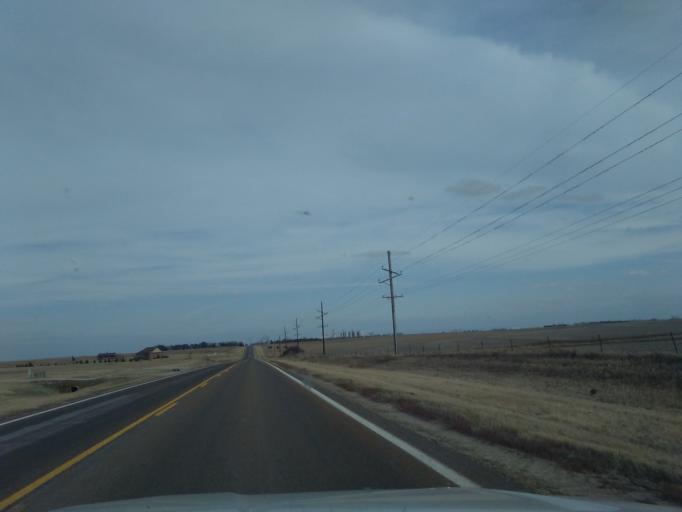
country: US
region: Nebraska
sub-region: Saline County
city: Wilber
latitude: 40.3061
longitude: -97.0274
